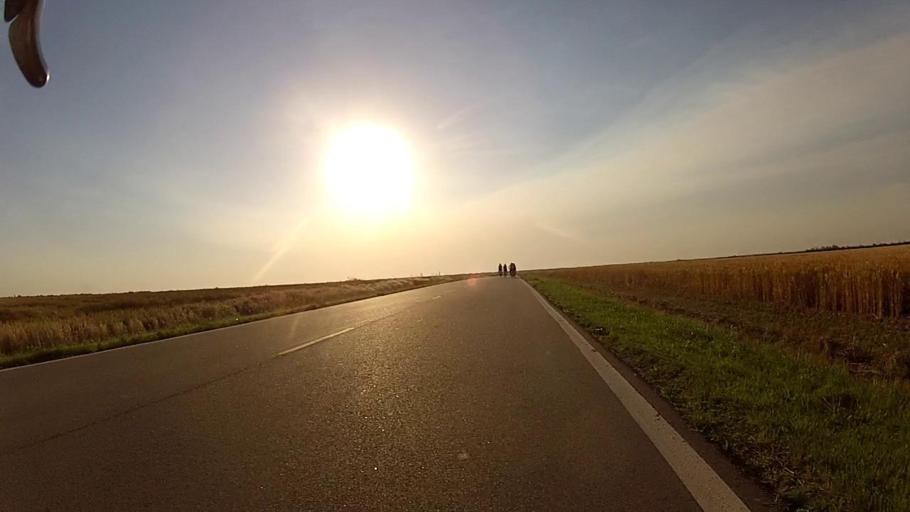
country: US
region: Kansas
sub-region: Harper County
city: Anthony
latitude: 37.1544
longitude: -97.8204
